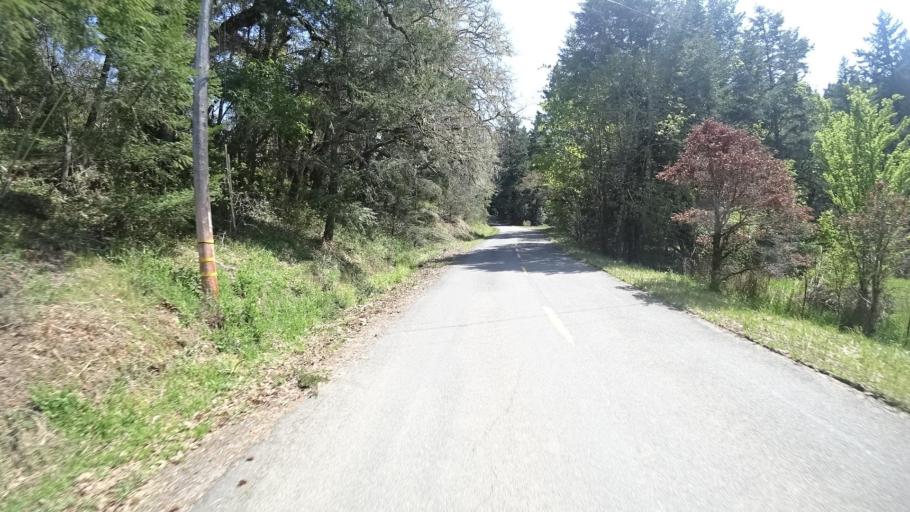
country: US
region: California
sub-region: Humboldt County
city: Redway
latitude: 40.2841
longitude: -123.6459
